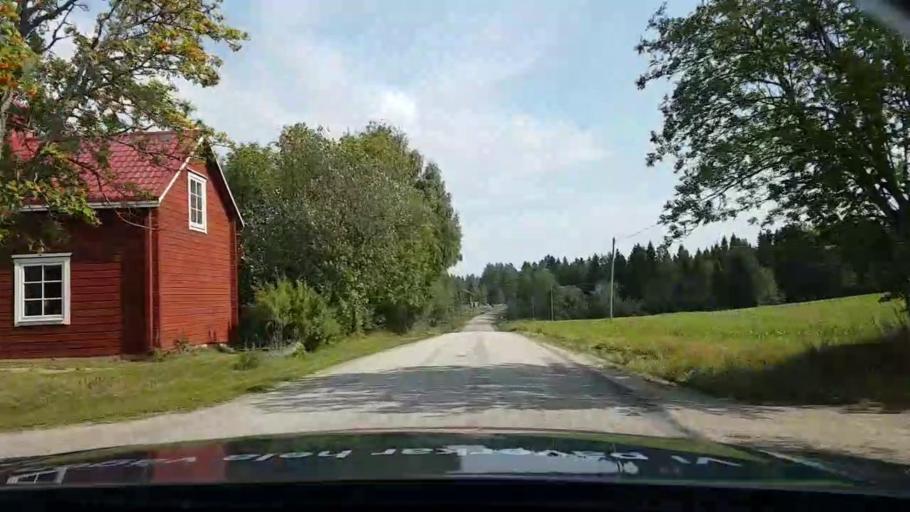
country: SE
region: Jaemtland
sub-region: Braecke Kommun
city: Braecke
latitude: 62.7294
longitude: 15.4865
